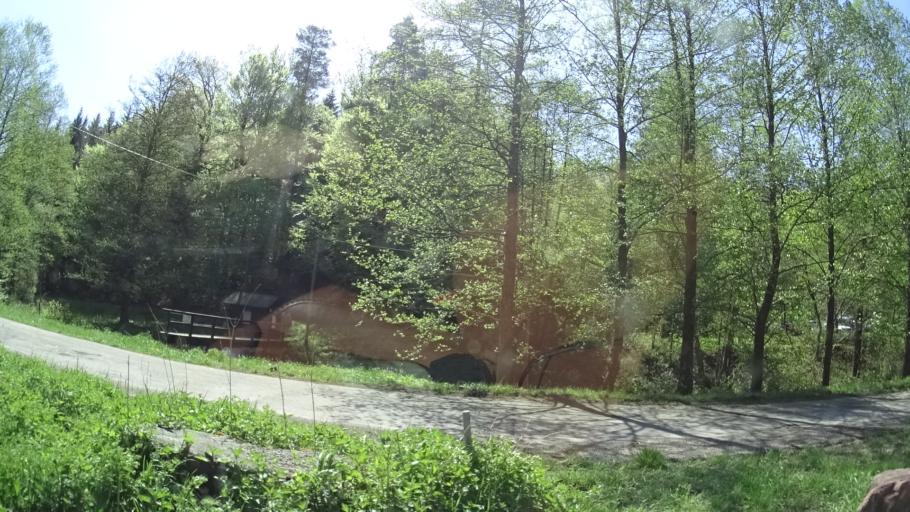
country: DE
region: Baden-Wuerttemberg
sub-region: Karlsruhe Region
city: Dobel
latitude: 48.7823
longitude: 8.5214
